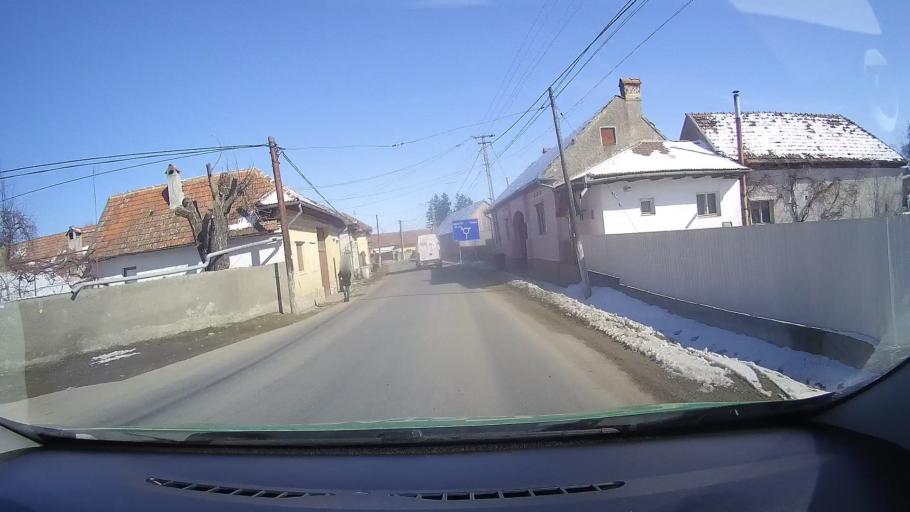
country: RO
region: Brasov
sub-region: Comuna Sambata de Sus
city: Sambata de Sus
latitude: 45.7598
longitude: 24.8264
